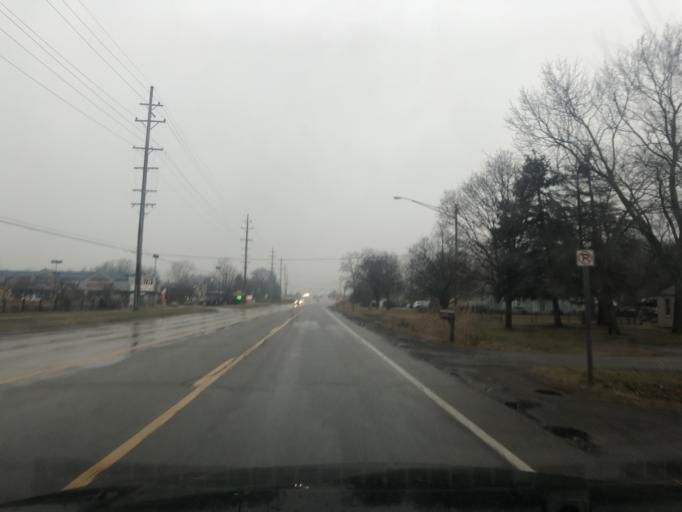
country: US
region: Michigan
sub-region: Wayne County
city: Rockwood
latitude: 42.0954
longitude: -83.2339
